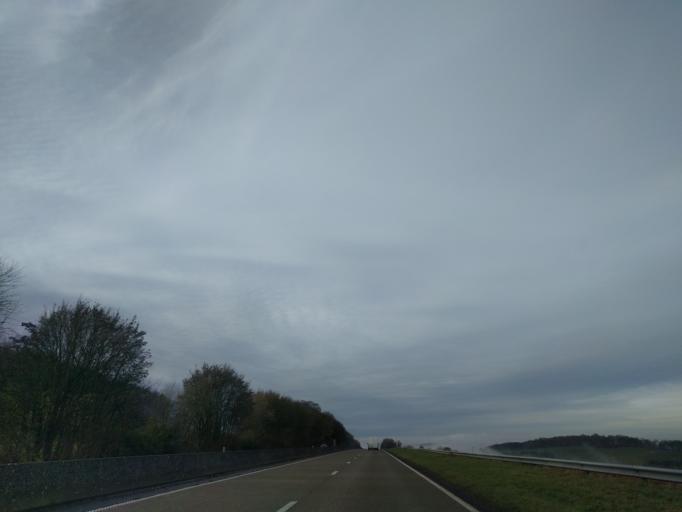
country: BE
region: Wallonia
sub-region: Province de Namur
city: Dinant
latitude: 50.2391
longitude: 4.9534
